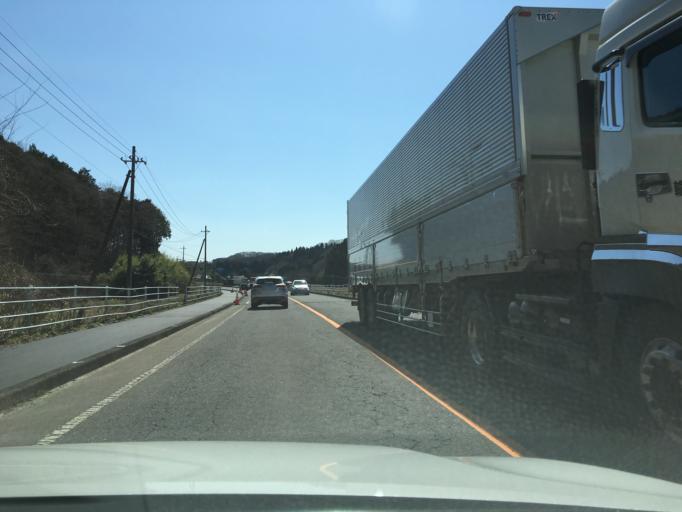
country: JP
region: Tochigi
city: Kuroiso
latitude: 37.0447
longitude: 140.1701
